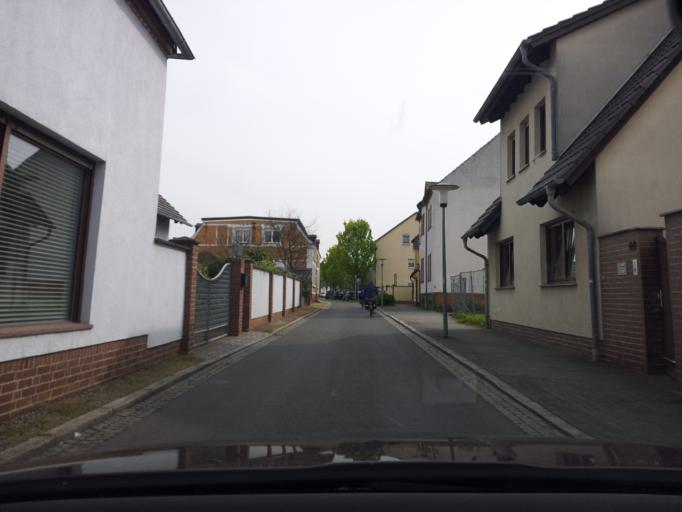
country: DE
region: Brandenburg
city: Lubbenau
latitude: 51.8672
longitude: 13.9560
